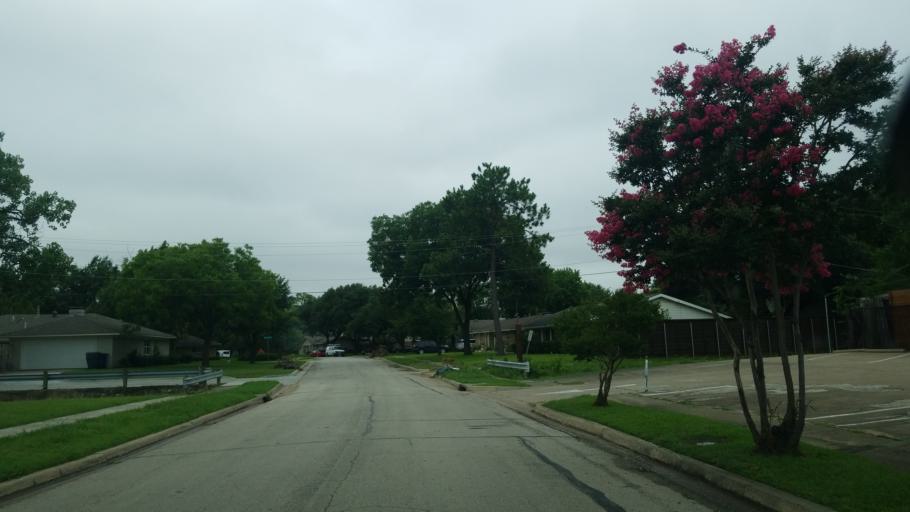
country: US
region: Texas
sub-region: Dallas County
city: Farmers Branch
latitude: 32.8992
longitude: -96.8636
